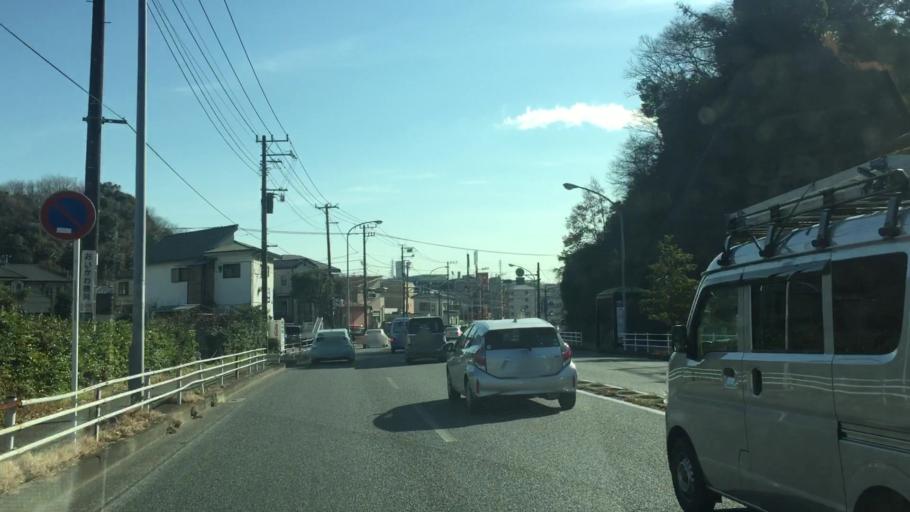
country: JP
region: Kanagawa
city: Zushi
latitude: 35.3498
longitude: 139.6076
